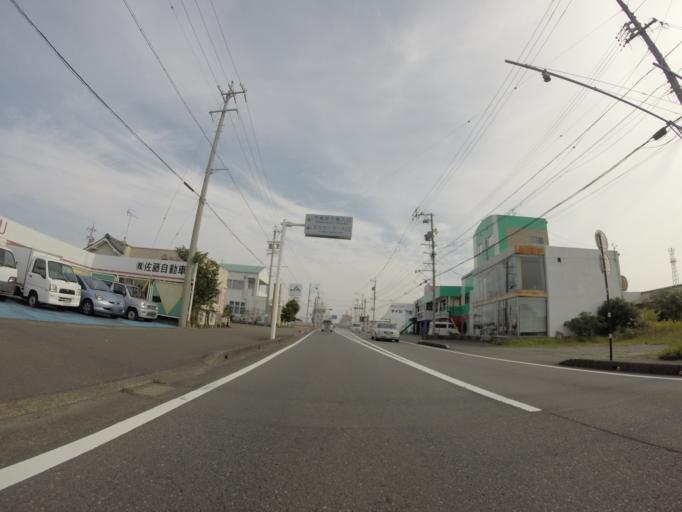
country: JP
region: Shizuoka
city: Sagara
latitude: 34.7365
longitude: 138.2293
